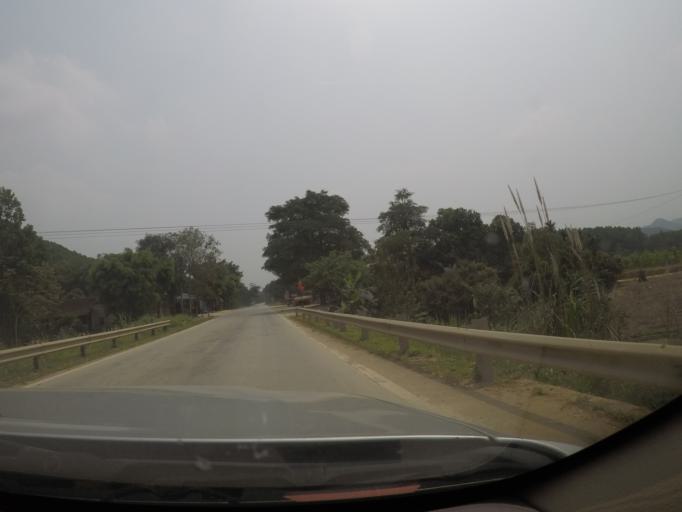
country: VN
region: Thanh Hoa
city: Thi Tran Yen Cat
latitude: 19.7593
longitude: 105.4185
